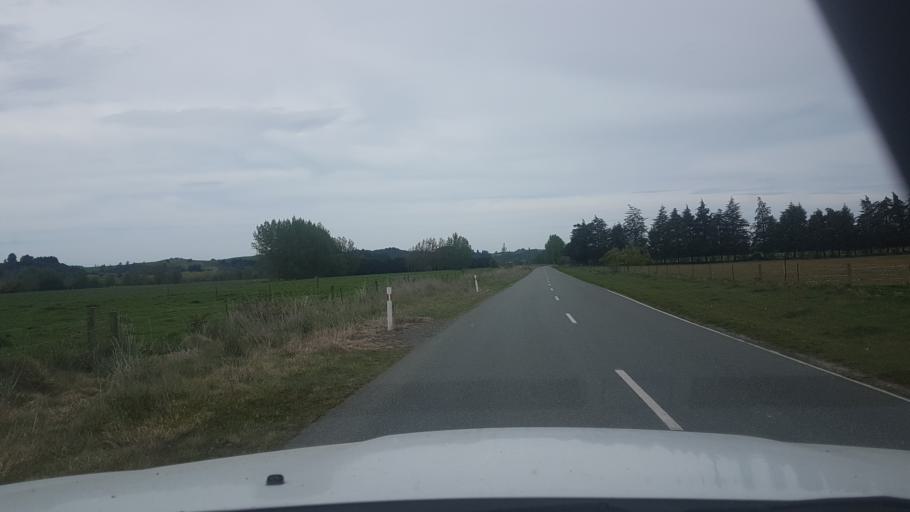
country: NZ
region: Canterbury
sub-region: Timaru District
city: Pleasant Point
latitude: -44.0728
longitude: 171.1657
